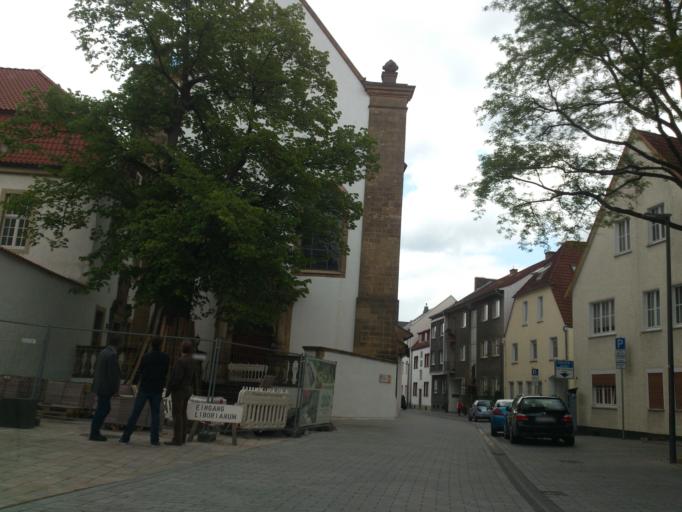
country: DE
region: North Rhine-Westphalia
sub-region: Regierungsbezirk Detmold
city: Paderborn
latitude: 51.7208
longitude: 8.7578
